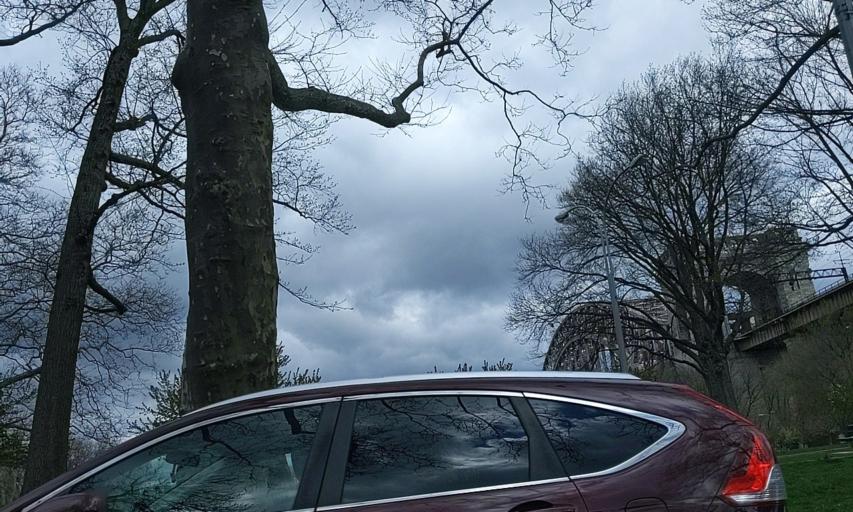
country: US
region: New York
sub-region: Queens County
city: Long Island City
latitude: 40.7798
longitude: -73.9198
